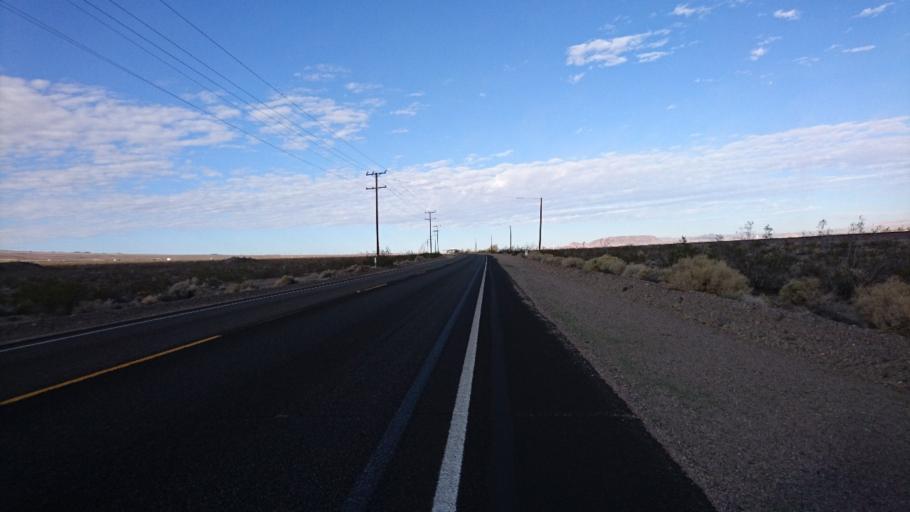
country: US
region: California
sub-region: San Bernardino County
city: Barstow
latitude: 34.8475
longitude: -116.7888
